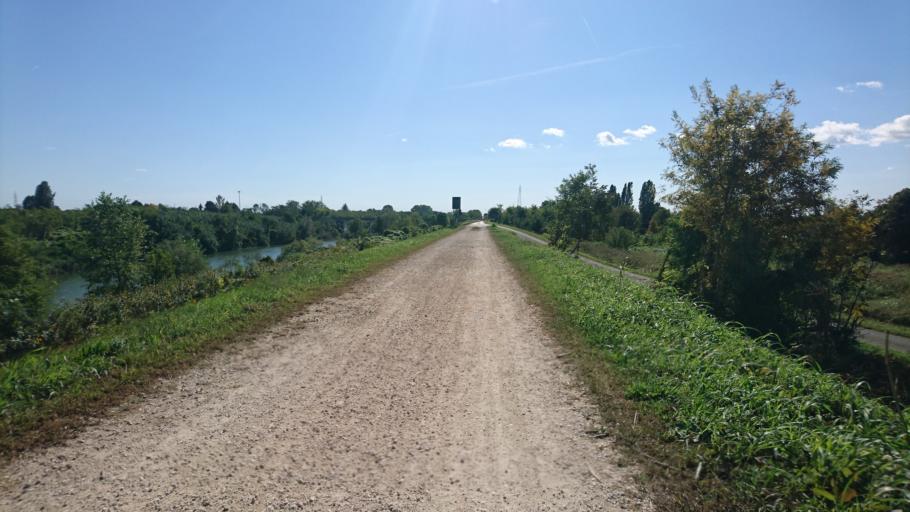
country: IT
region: Veneto
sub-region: Provincia di Venezia
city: Vigonovo
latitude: 45.3887
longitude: 12.0133
